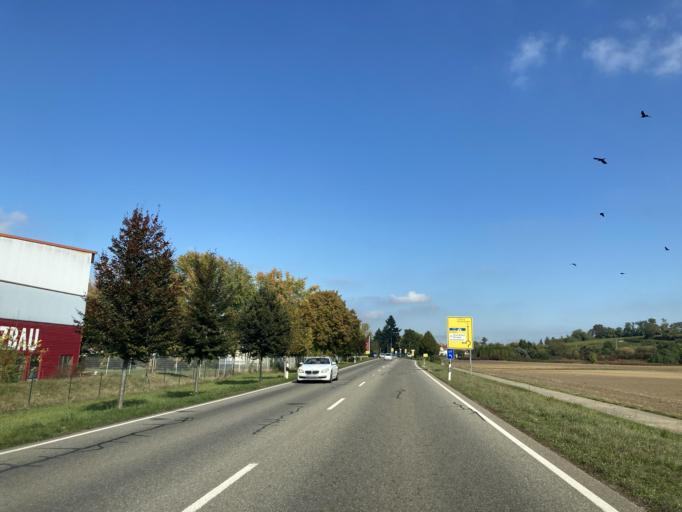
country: DE
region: Baden-Wuerttemberg
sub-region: Freiburg Region
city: Heitersheim
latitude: 47.8705
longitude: 7.6495
